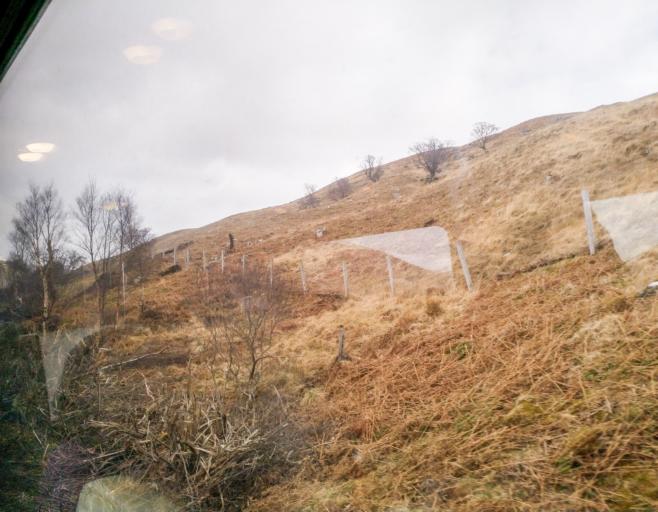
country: GB
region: Scotland
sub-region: Highland
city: Spean Bridge
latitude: 56.7797
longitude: -4.7329
